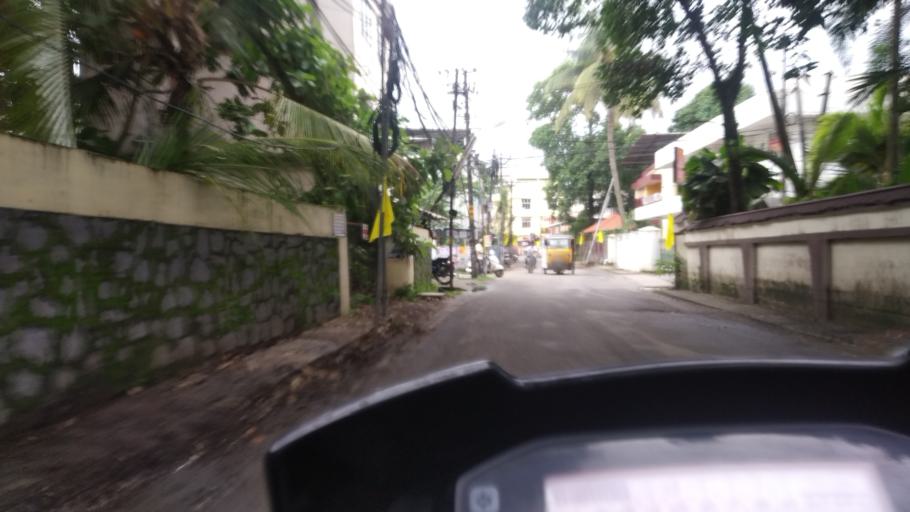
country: IN
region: Kerala
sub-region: Ernakulam
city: Cochin
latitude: 9.9922
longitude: 76.2962
